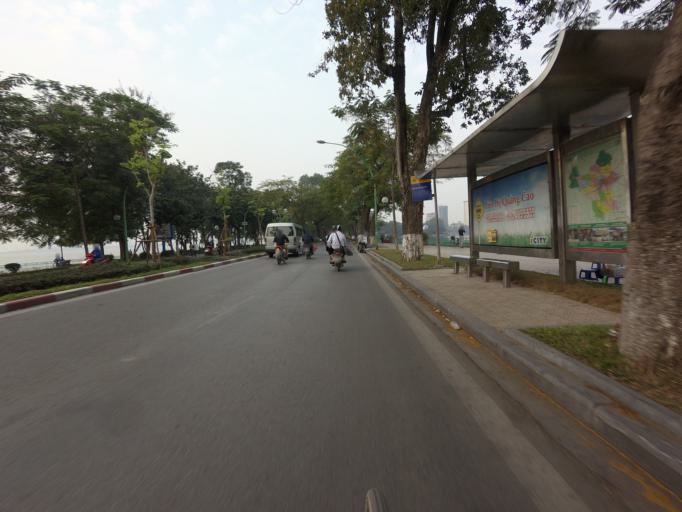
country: VN
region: Ha Noi
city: Hanoi
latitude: 21.0447
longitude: 105.8364
